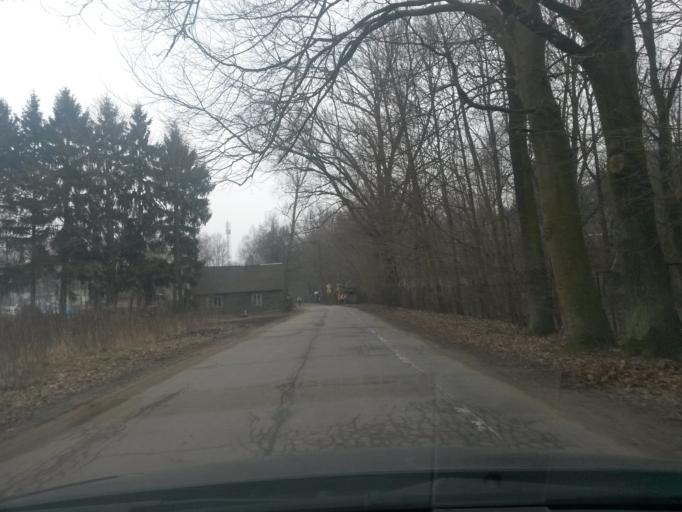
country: PL
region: Masovian Voivodeship
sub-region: Powiat legionowski
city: Serock
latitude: 52.4930
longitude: 21.0568
